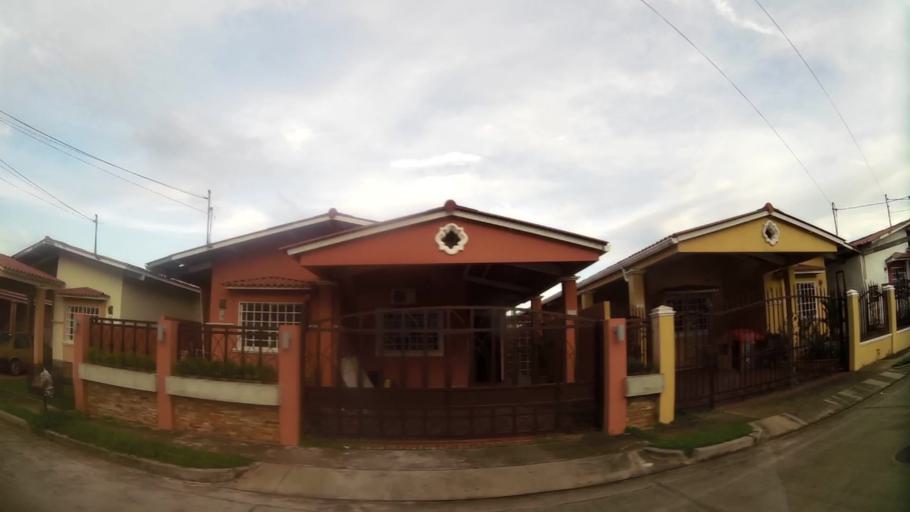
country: PA
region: Panama
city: La Chorrera
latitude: 8.8687
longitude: -79.7637
